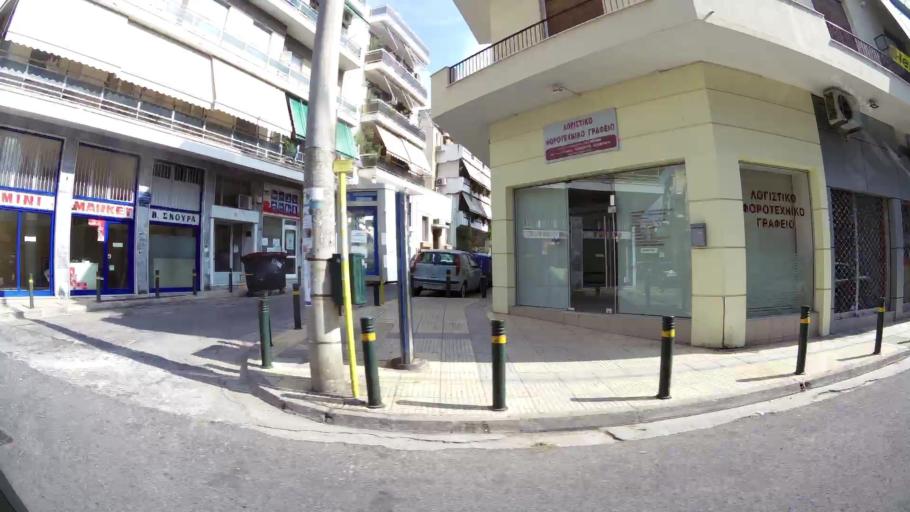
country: GR
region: Attica
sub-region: Nomarchia Athinas
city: Athens
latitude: 37.9981
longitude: 23.7156
